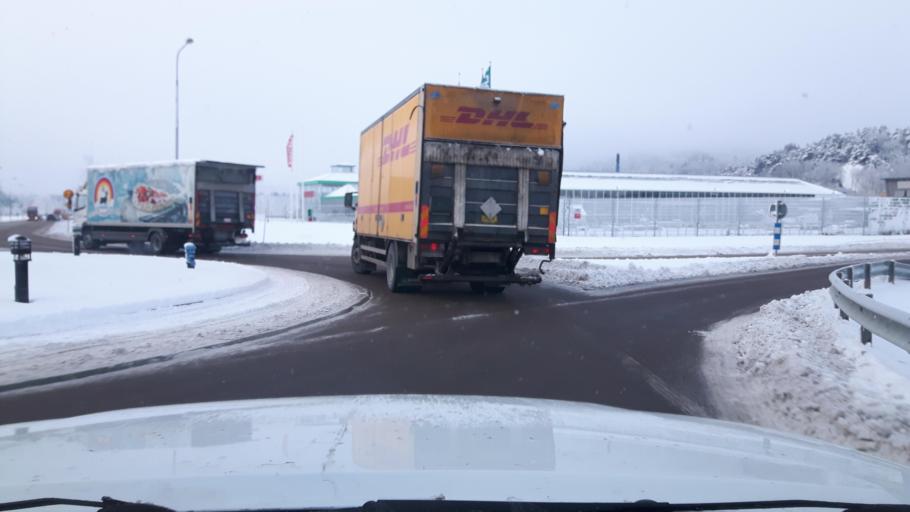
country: SE
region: Halland
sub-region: Kungsbacka Kommun
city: Kungsbacka
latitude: 57.5112
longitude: 12.0716
